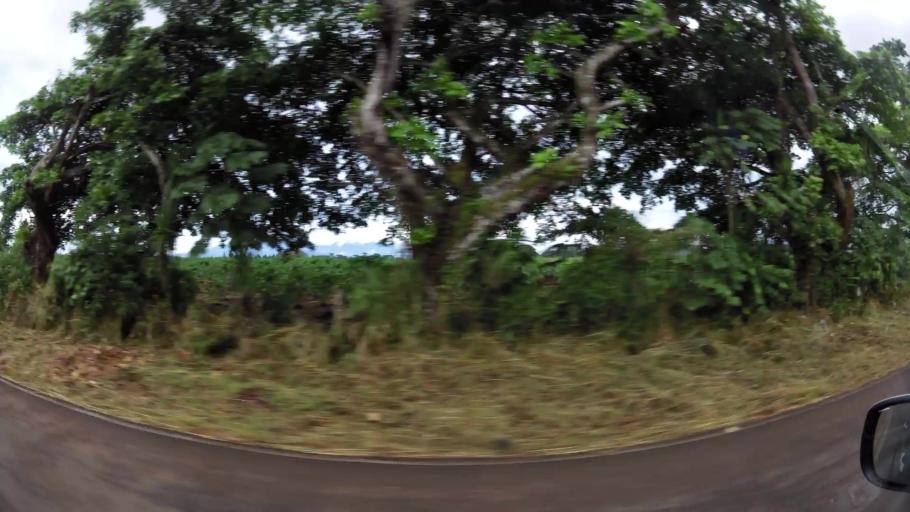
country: CR
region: Puntarenas
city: Esparza
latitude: 9.9922
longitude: -84.6377
